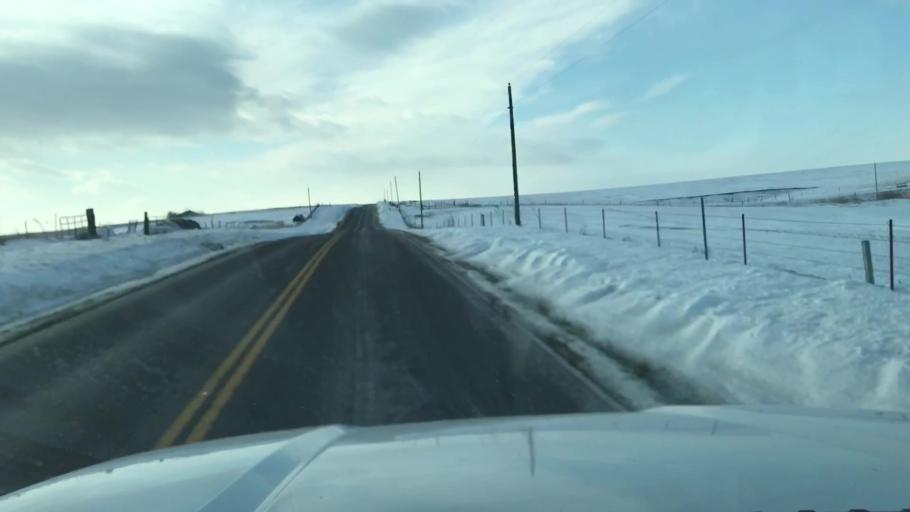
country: US
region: Missouri
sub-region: Nodaway County
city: Maryville
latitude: 40.2010
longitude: -94.9034
